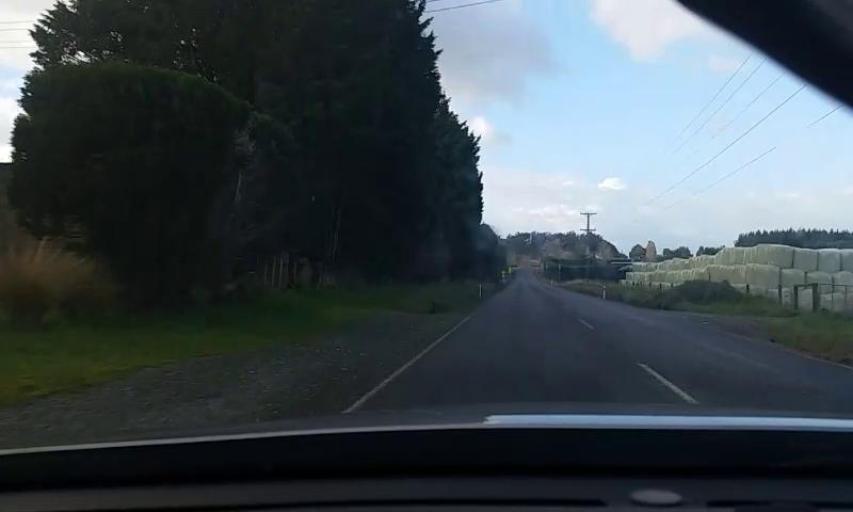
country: NZ
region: Southland
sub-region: Invercargill City
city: Invercargill
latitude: -46.3806
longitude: 168.4326
